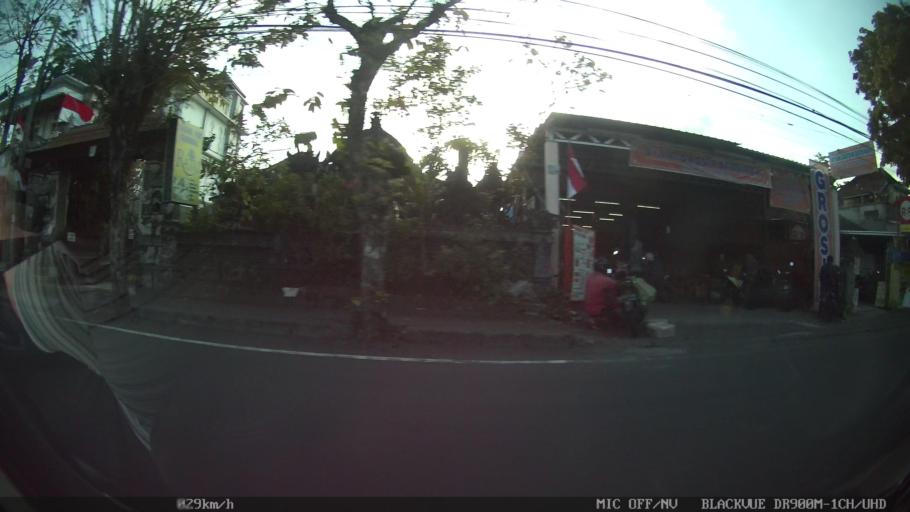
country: ID
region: Bali
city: Banjar Kertasari
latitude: -8.6263
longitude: 115.2076
